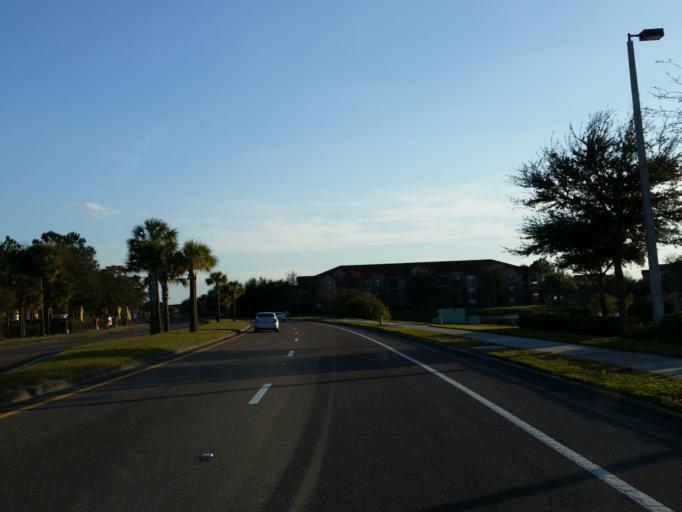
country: US
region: Florida
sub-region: Hillsborough County
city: Brandon
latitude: 27.9188
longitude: -82.3235
